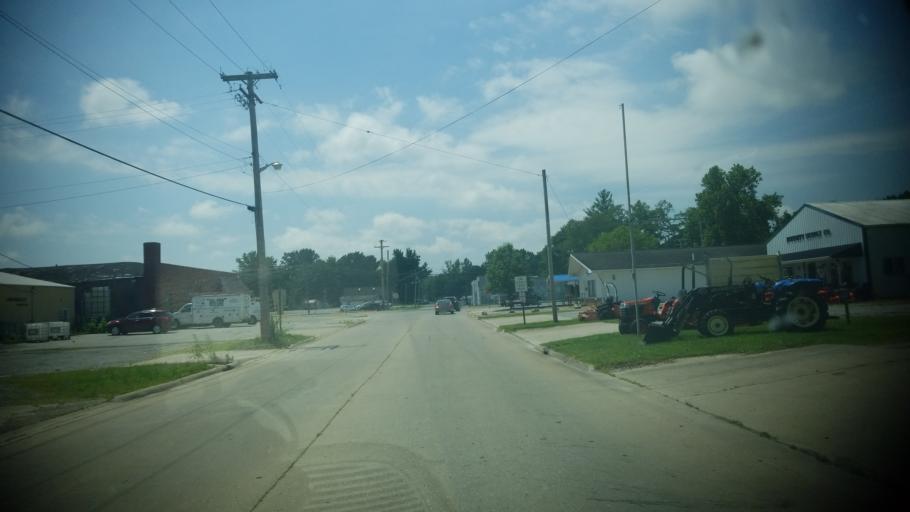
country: US
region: Illinois
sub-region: Wayne County
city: Fairfield
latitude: 38.3800
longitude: -88.3538
